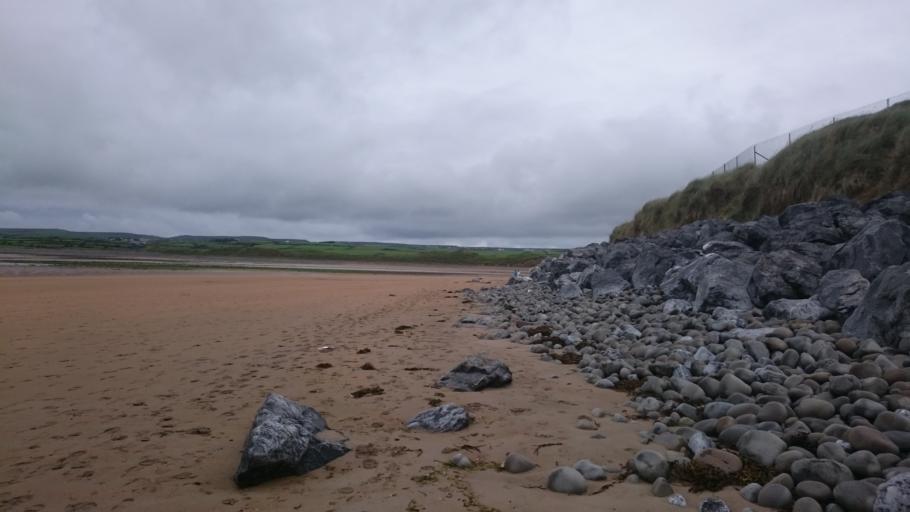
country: IE
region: Munster
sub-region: An Clar
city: Kilrush
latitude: 52.9407
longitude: -9.3579
